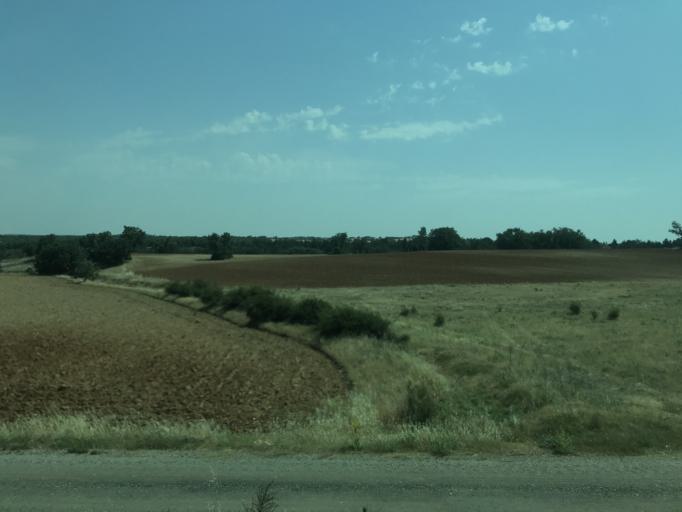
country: ES
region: Castille and Leon
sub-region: Provincia de Segovia
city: Boceguillas
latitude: 41.3186
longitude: -3.6278
